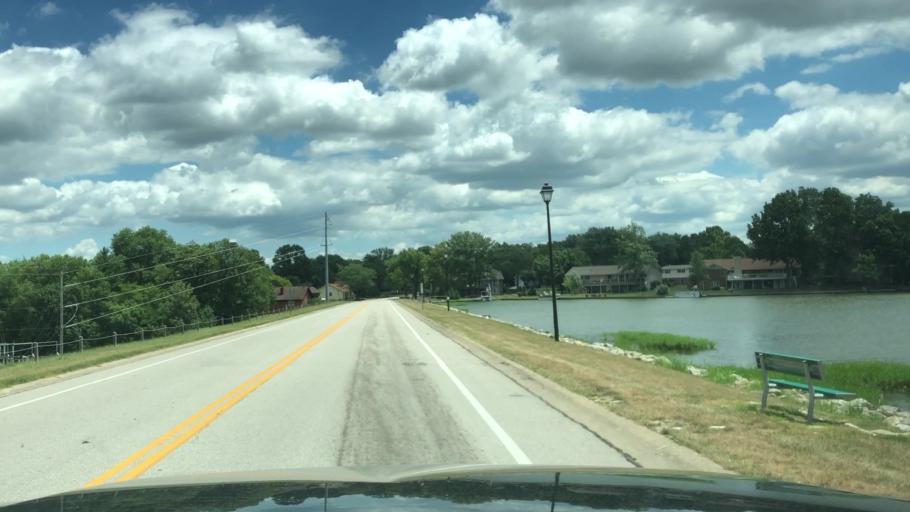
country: US
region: Missouri
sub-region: Saint Charles County
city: Lake Saint Louis
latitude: 38.8007
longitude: -90.7915
